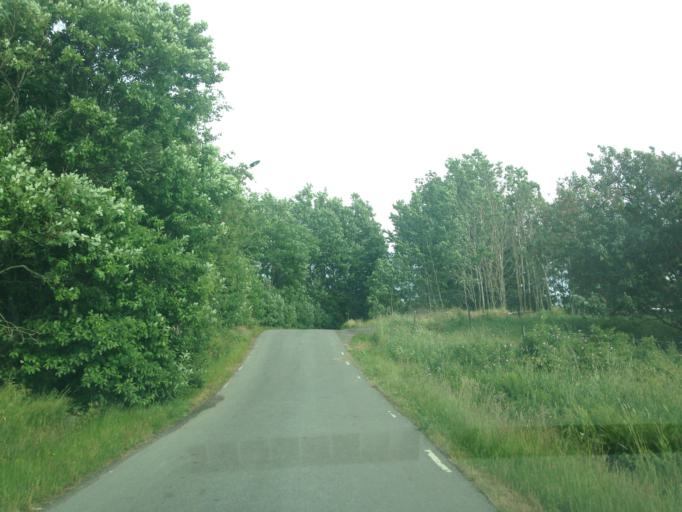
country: SE
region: Vaestra Goetaland
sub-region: Goteborg
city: Majorna
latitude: 57.7568
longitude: 11.8639
